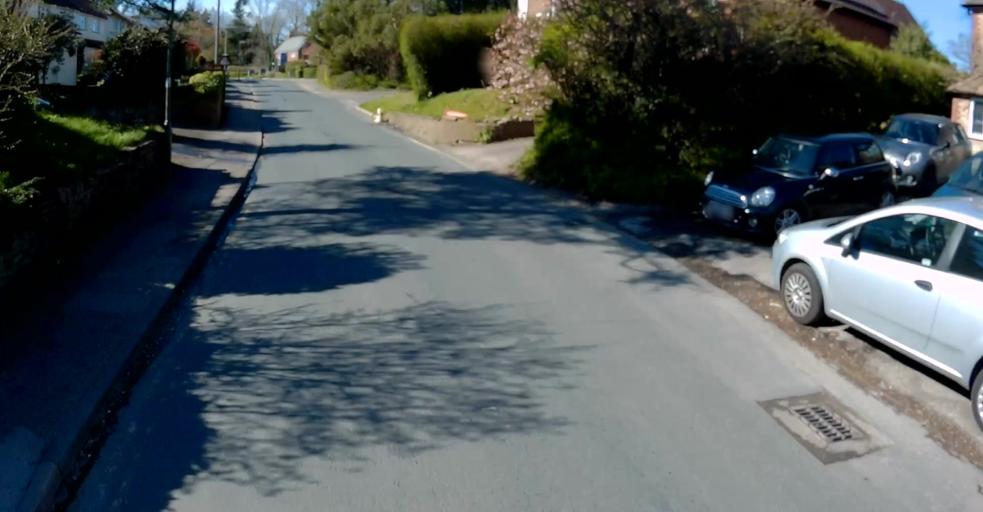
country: GB
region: England
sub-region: Surrey
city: Farnham
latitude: 51.2131
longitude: -0.8092
